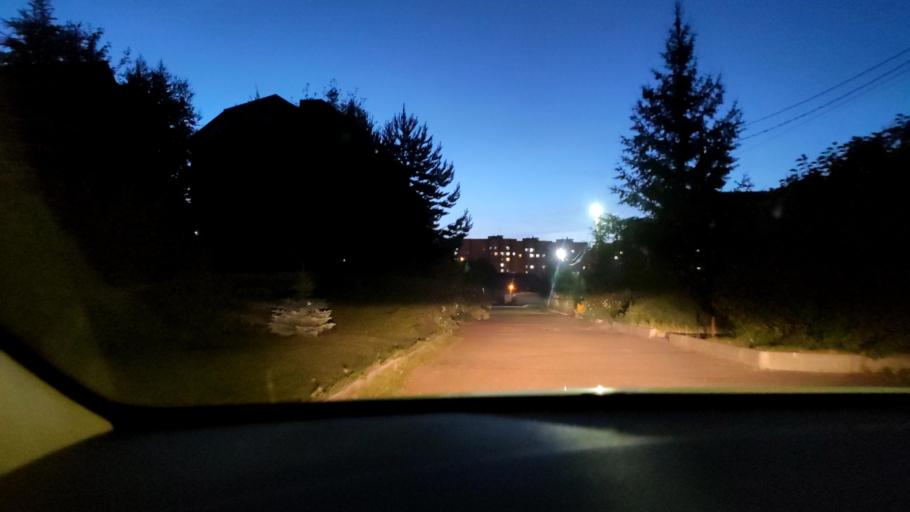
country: RU
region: Tatarstan
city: Stolbishchi
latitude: 55.7460
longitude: 49.2465
